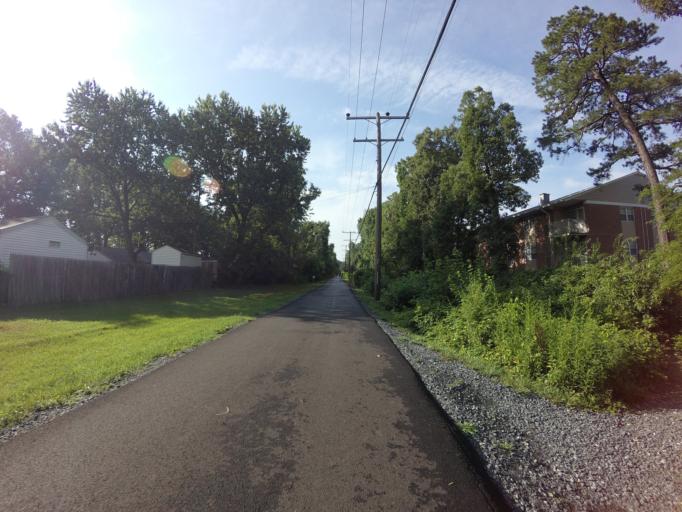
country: US
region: Maryland
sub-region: Anne Arundel County
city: Glen Burnie
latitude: 39.1495
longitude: -76.6156
